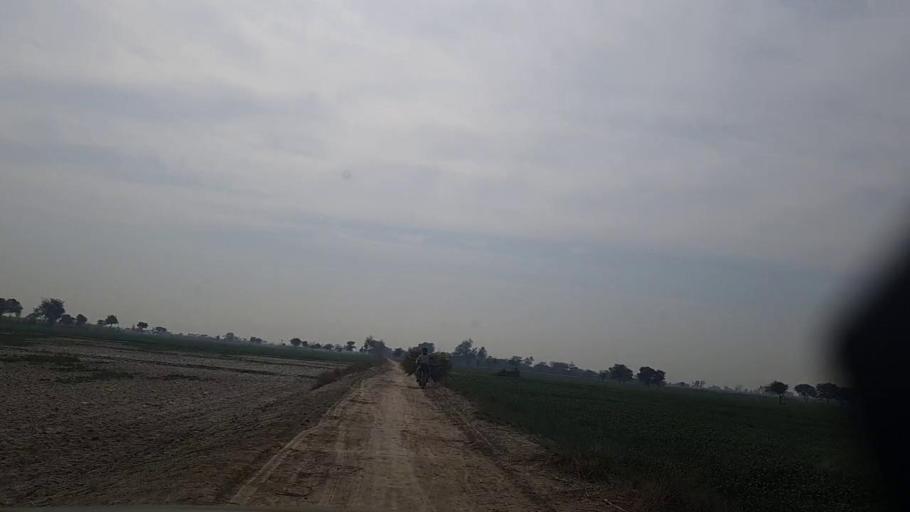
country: PK
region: Sindh
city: Sakrand
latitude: 26.2302
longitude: 68.2970
